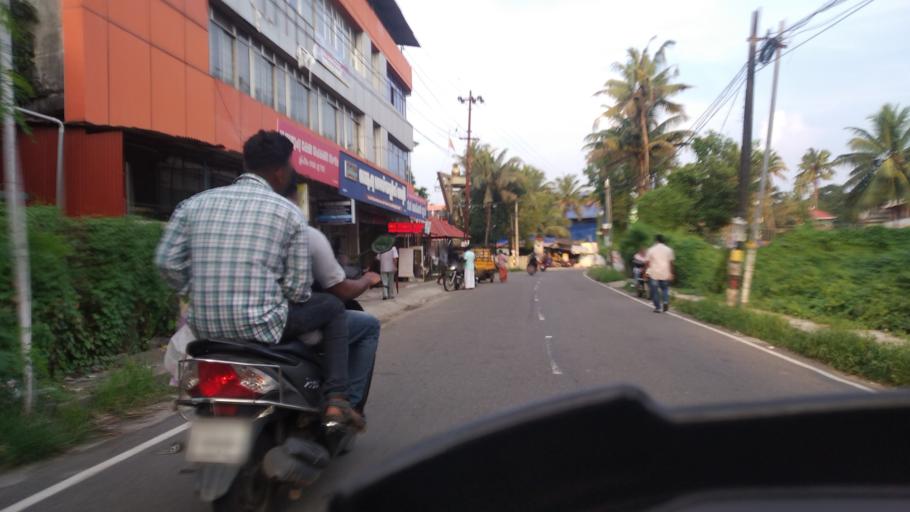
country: IN
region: Kerala
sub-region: Ernakulam
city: Elur
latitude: 10.0187
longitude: 76.2861
